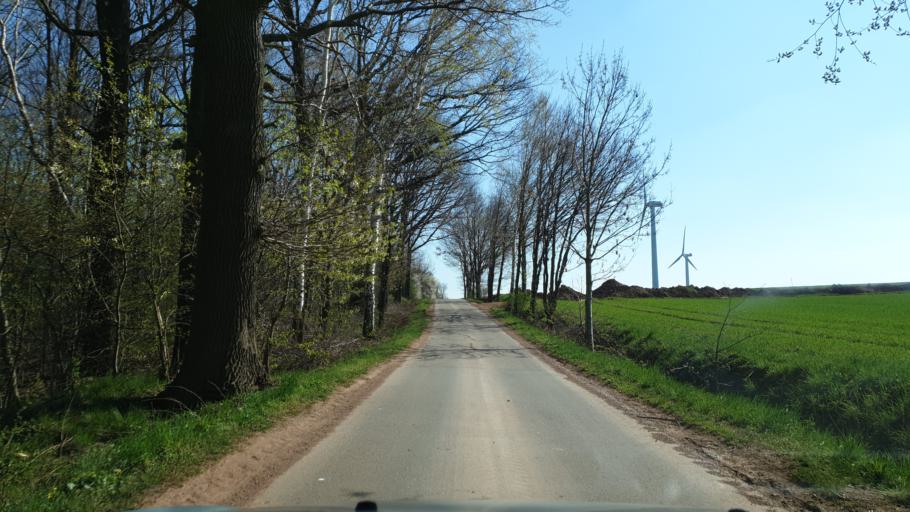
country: DE
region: Saxony
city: Hohndorf
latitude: 50.7598
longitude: 12.6854
